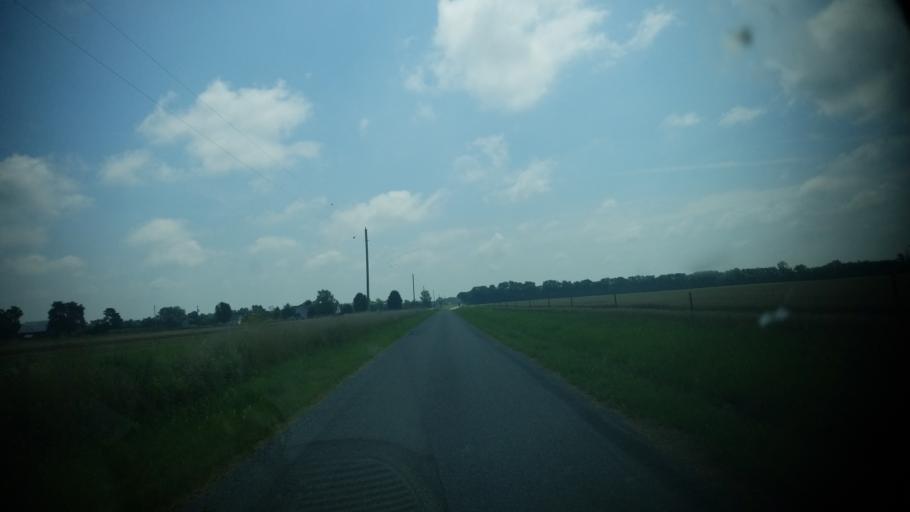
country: US
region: Illinois
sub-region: Wayne County
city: Fairfield
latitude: 38.5300
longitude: -88.3869
